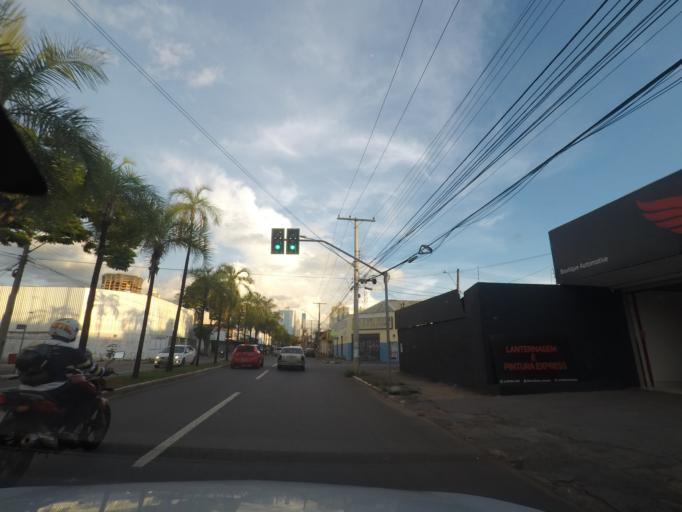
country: BR
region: Goias
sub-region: Goiania
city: Goiania
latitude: -16.6835
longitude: -49.2815
